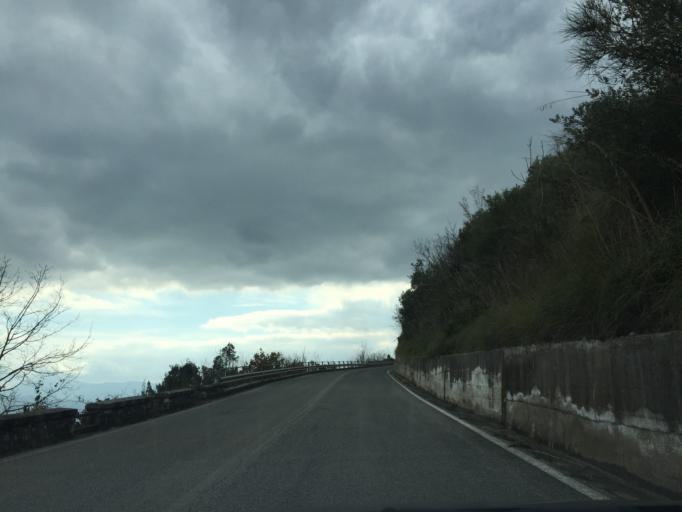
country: IT
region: Latium
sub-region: Provincia di Frosinone
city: Cassino
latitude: 41.4879
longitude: 13.8189
